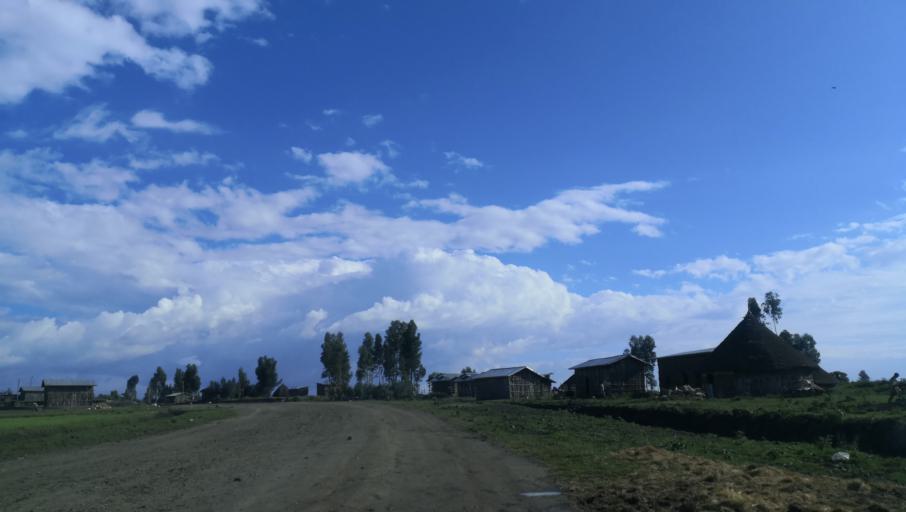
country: ET
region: Oromiya
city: Tulu Bolo
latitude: 8.5496
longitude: 38.2495
